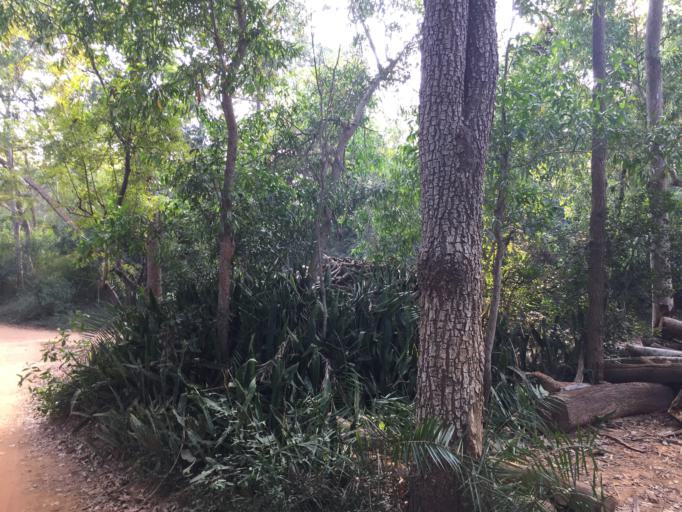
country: IN
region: Tamil Nadu
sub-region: Villupuram
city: Auroville
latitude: 11.9946
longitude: 79.8217
